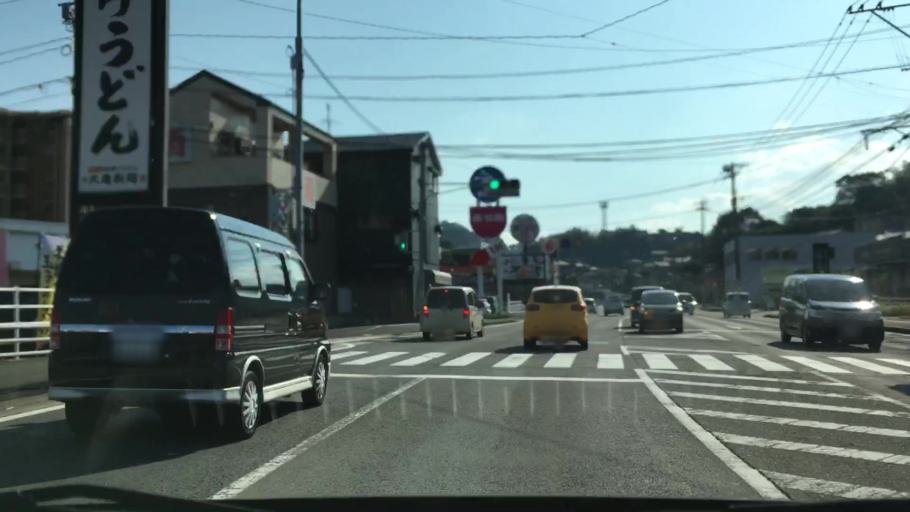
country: JP
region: Nagasaki
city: Togitsu
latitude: 32.8392
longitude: 129.8378
